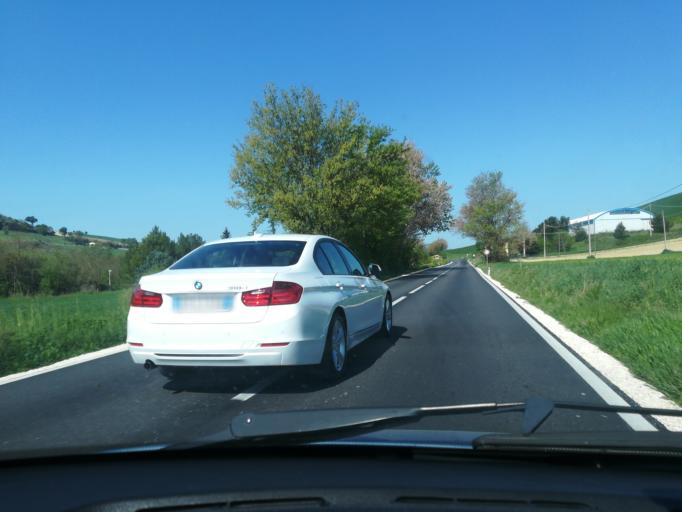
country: IT
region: The Marches
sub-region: Provincia di Macerata
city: Villa Potenza
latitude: 43.3281
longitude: 13.3950
